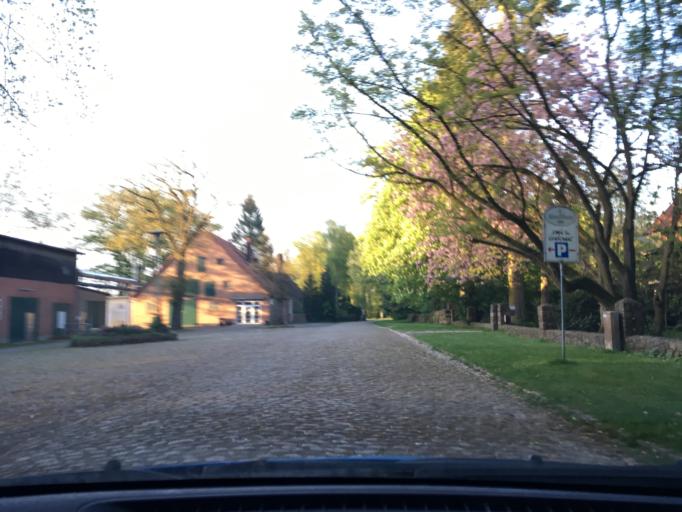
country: DE
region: Lower Saxony
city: Amelinghausen
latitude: 53.1243
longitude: 10.1897
